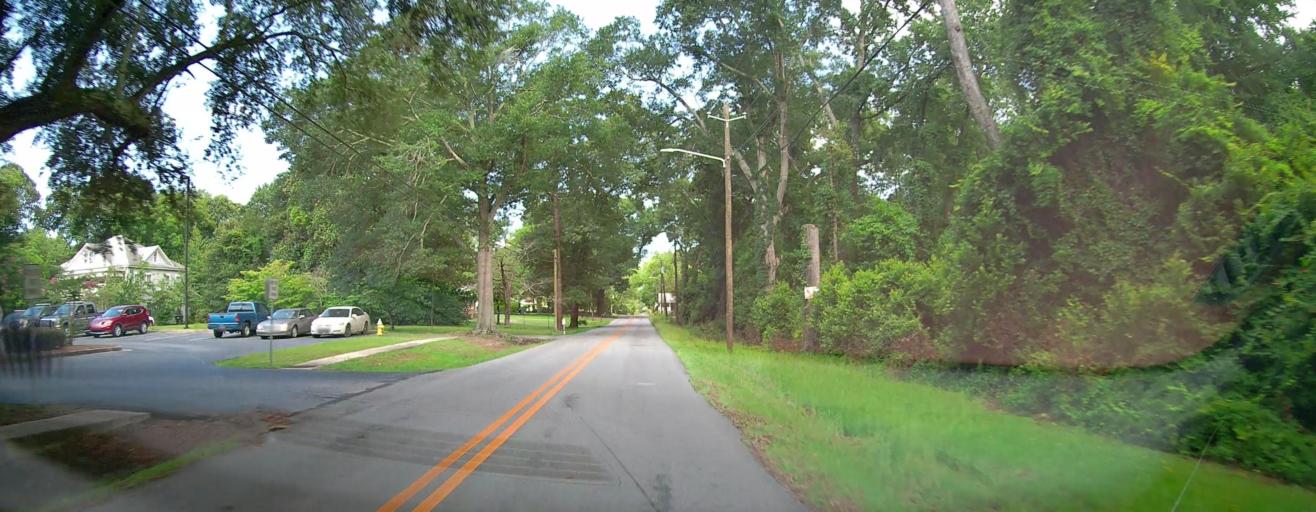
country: US
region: Georgia
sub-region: Peach County
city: Byron
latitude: 32.6549
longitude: -83.7620
